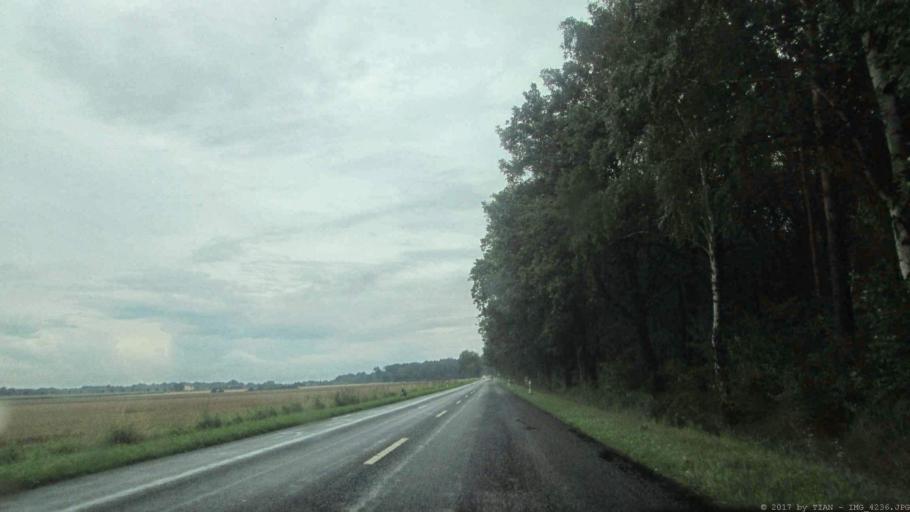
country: DE
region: Lower Saxony
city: Danndorf
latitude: 52.4191
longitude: 10.8919
